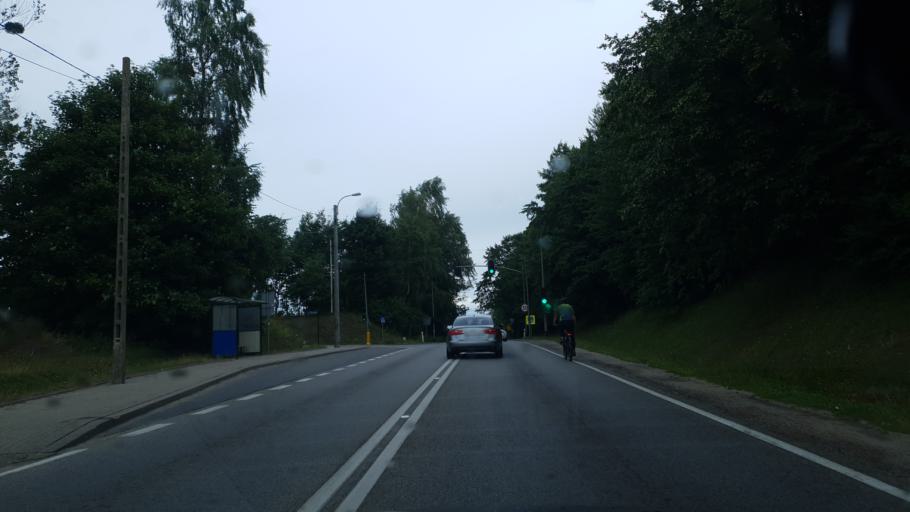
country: PL
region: Pomeranian Voivodeship
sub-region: Powiat kartuski
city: Chwaszczyno
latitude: 54.4515
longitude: 18.4390
